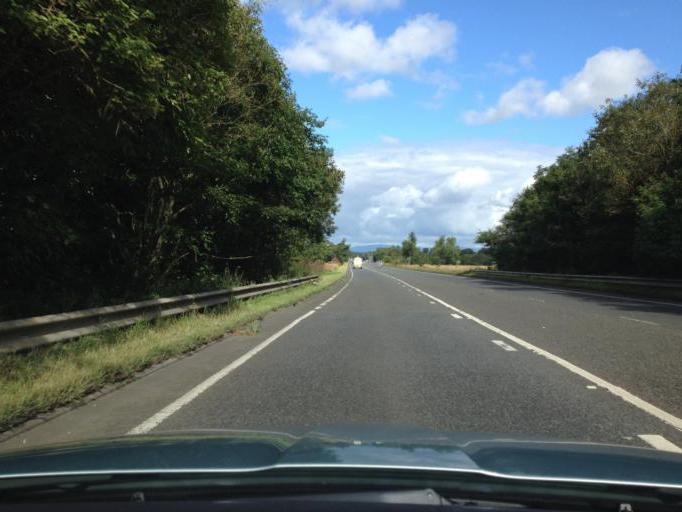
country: GB
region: Scotland
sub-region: West Lothian
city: Bathgate
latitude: 55.9120
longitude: -3.6753
